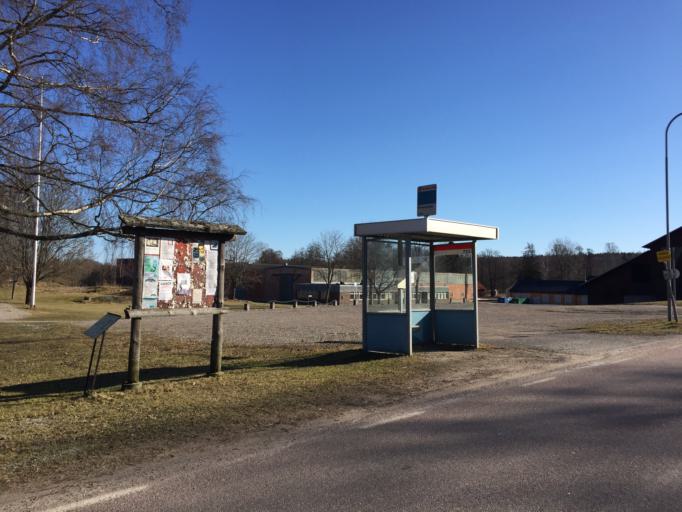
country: SE
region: OErebro
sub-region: Orebro Kommun
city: Odensbacken
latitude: 59.0154
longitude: 15.5790
